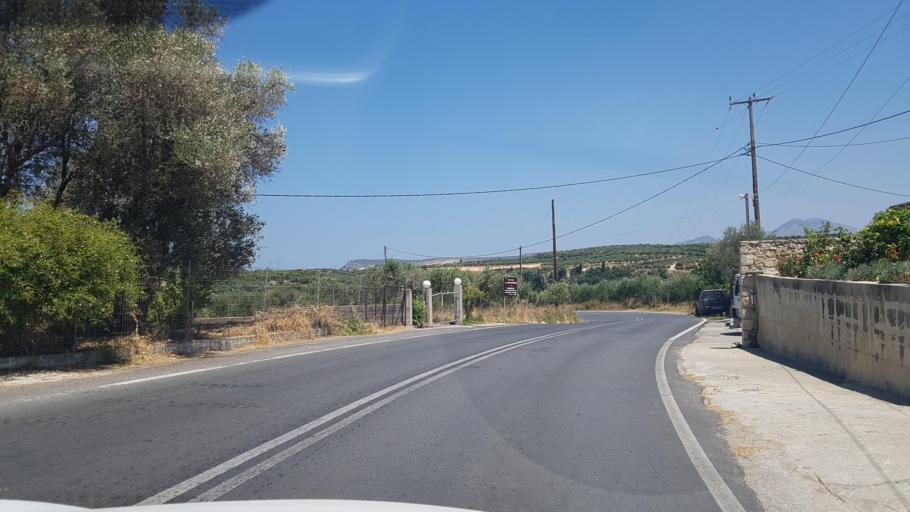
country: GR
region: Crete
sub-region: Nomos Rethymnis
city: Agia Foteini
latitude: 35.3545
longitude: 24.5883
